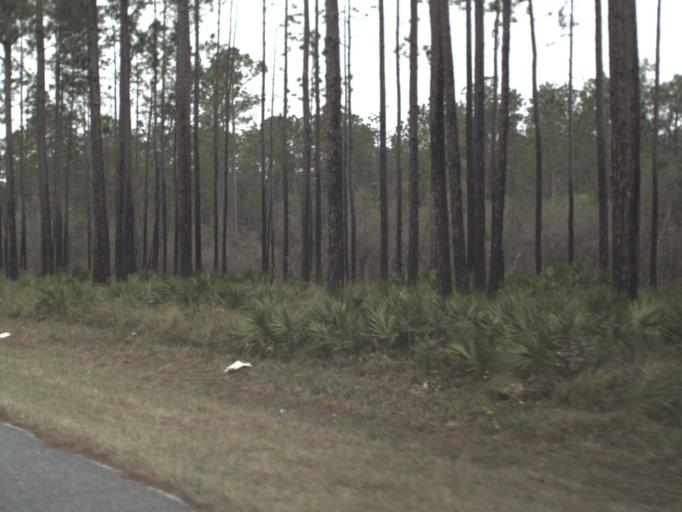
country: US
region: Florida
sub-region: Franklin County
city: Apalachicola
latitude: 29.9280
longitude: -84.9771
